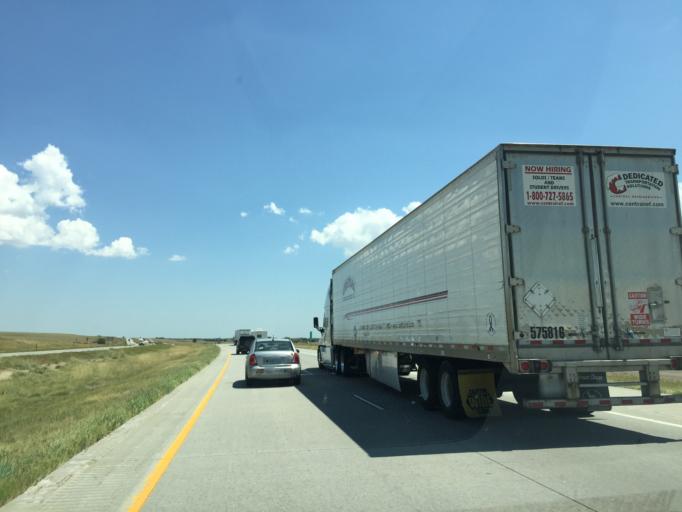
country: US
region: Colorado
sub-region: Lincoln County
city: Limon
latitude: 39.2875
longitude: -103.7890
